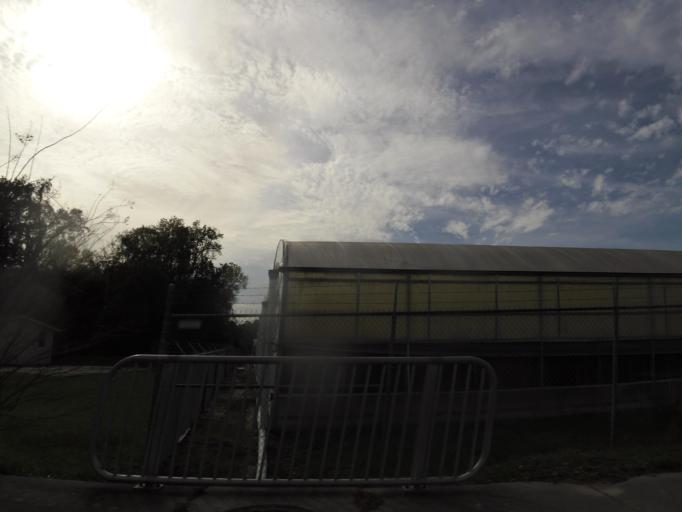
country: US
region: Florida
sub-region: Clay County
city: Bellair-Meadowbrook Terrace
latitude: 30.2718
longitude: -81.7715
